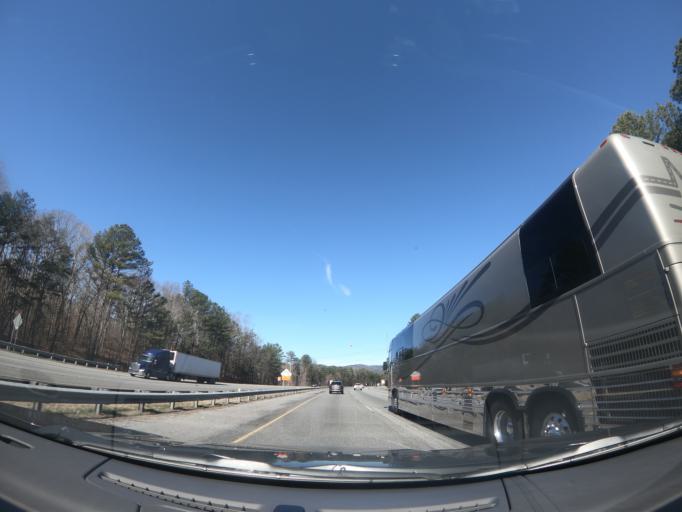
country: US
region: Georgia
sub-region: Whitfield County
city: Dalton
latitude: 34.6685
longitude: -84.9949
